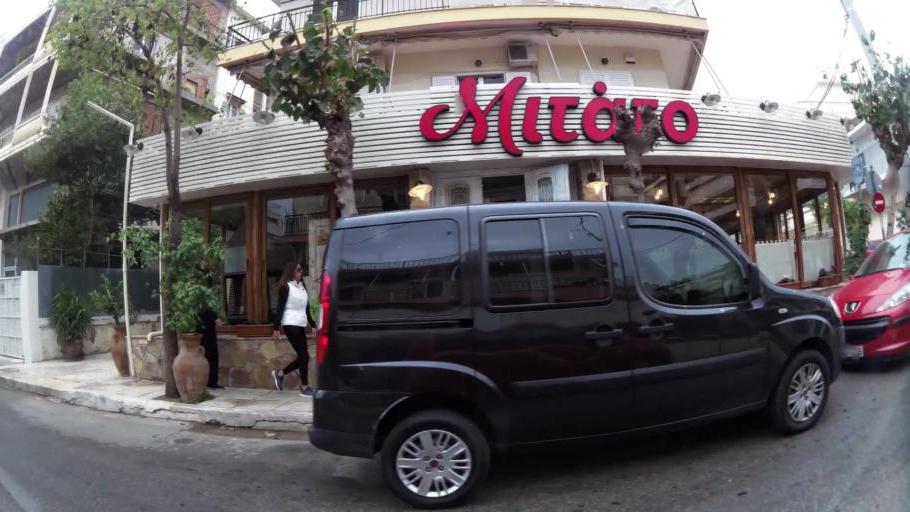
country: GR
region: Attica
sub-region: Nomarchia Athinas
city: Ilion
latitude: 38.0277
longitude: 23.7017
